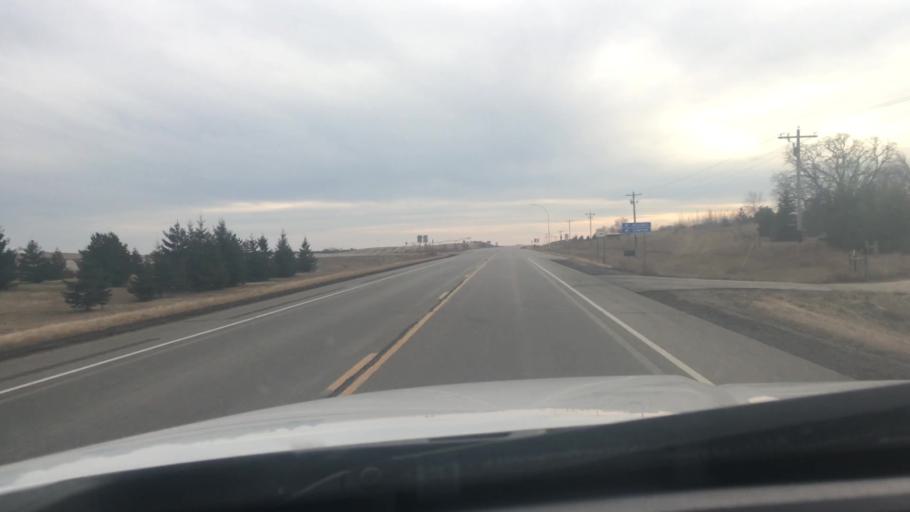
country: US
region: Minnesota
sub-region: Otter Tail County
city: Perham
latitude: 46.3128
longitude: -95.7184
